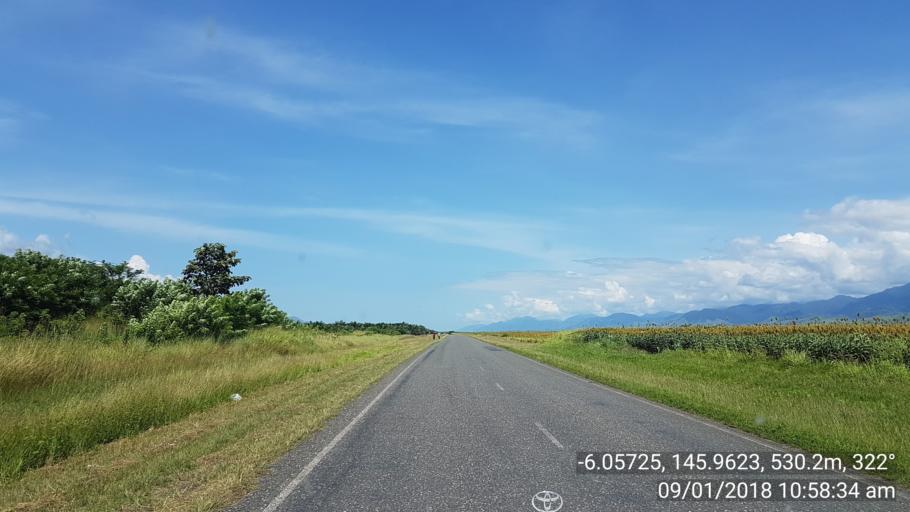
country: PG
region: Eastern Highlands
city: Kainantu
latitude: -6.0573
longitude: 145.9622
